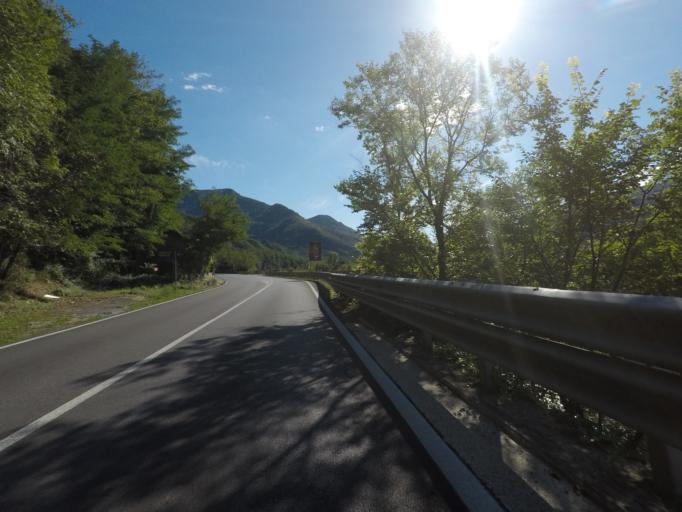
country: IT
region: Tuscany
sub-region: Provincia di Lucca
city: Borgo a Mozzano
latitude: 43.9805
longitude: 10.5523
